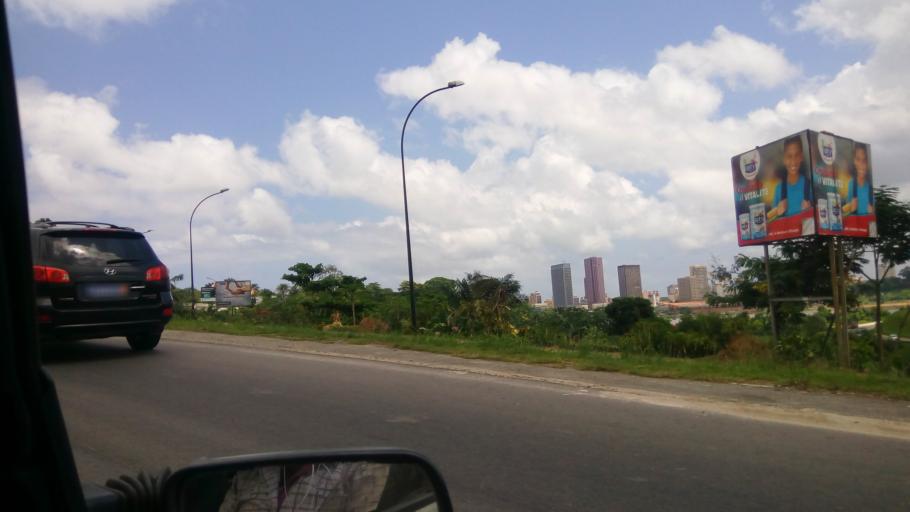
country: CI
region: Lagunes
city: Abidjan
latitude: 5.3368
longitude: -4.0097
